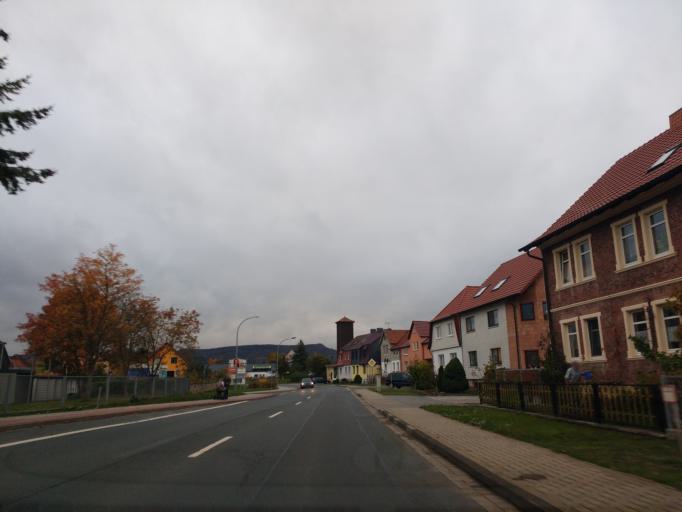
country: DE
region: Thuringia
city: Grossbodungen
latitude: 51.4775
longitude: 10.4861
